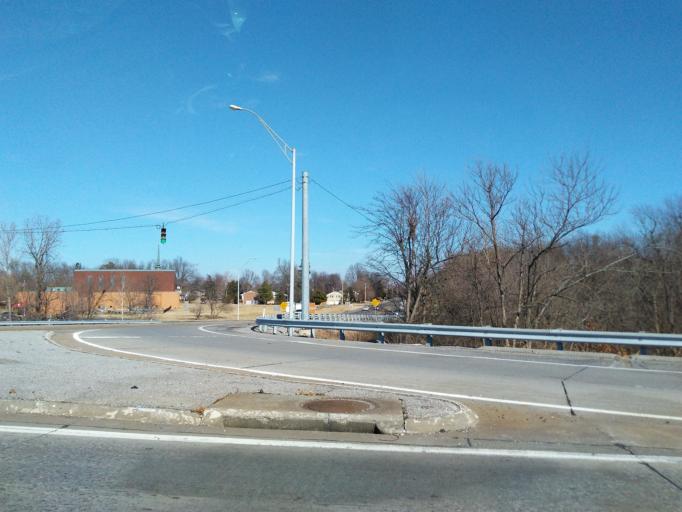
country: US
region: Kentucky
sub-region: McCracken County
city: Hendron
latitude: 37.0576
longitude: -88.6538
